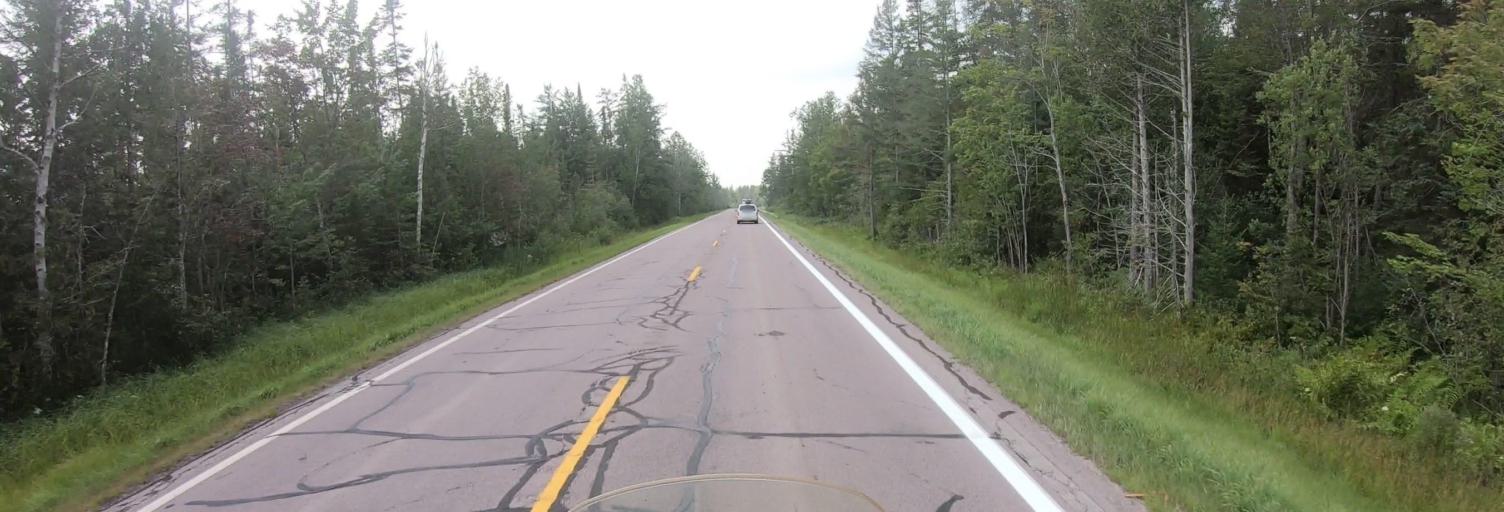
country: US
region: Michigan
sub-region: Luce County
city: Newberry
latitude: 46.4669
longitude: -85.4336
